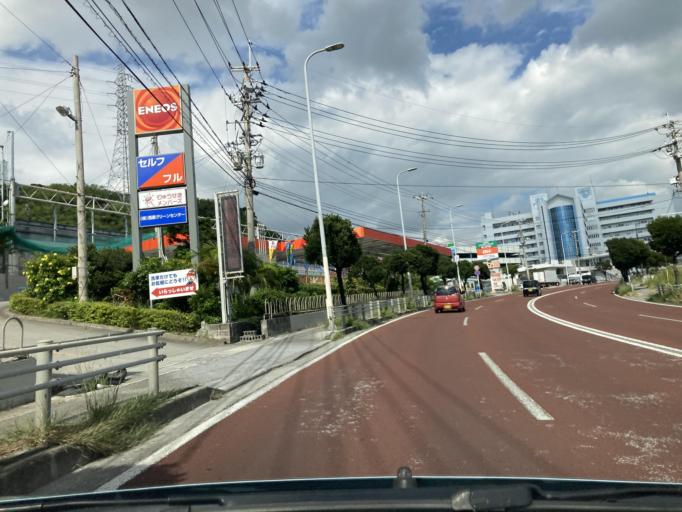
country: JP
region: Okinawa
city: Ginowan
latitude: 26.2361
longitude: 127.7697
